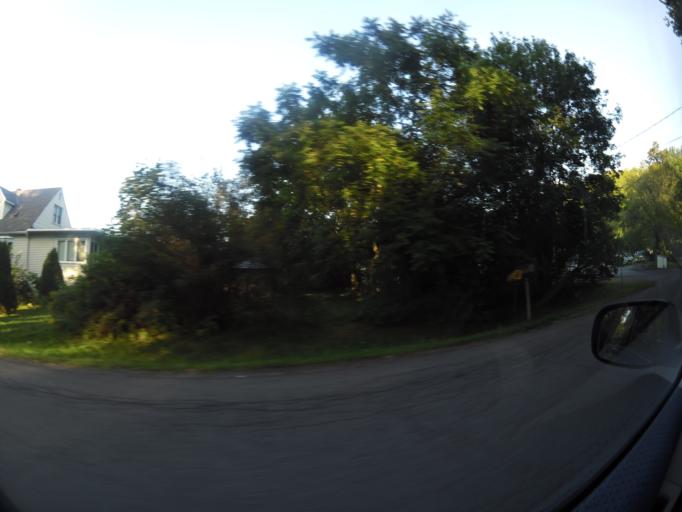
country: CA
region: Ontario
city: Clarence-Rockland
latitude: 45.5076
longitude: -75.4245
